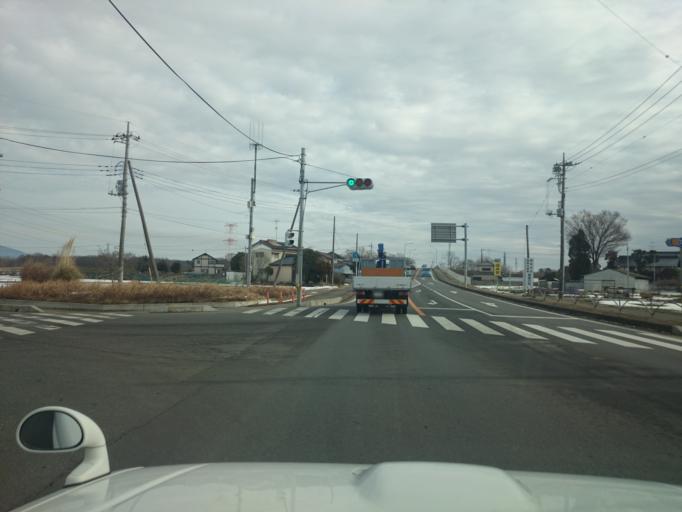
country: JP
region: Ibaraki
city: Ishige
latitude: 36.1107
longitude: 139.9952
